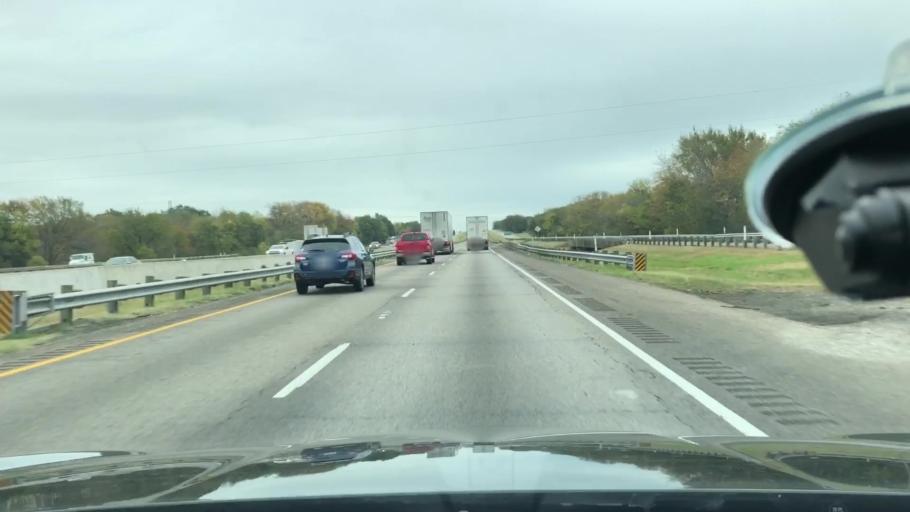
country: US
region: Texas
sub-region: Hopkins County
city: Sulphur Springs
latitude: 33.1457
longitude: -95.5538
